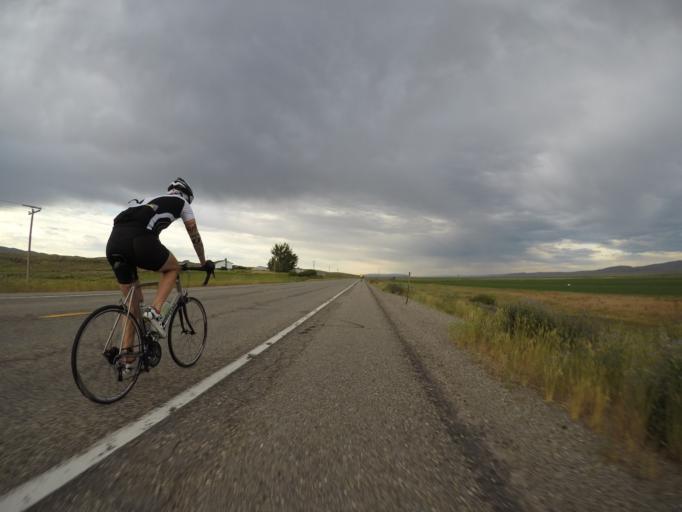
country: US
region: Utah
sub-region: Rich County
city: Randolph
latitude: 41.9799
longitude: -110.9428
